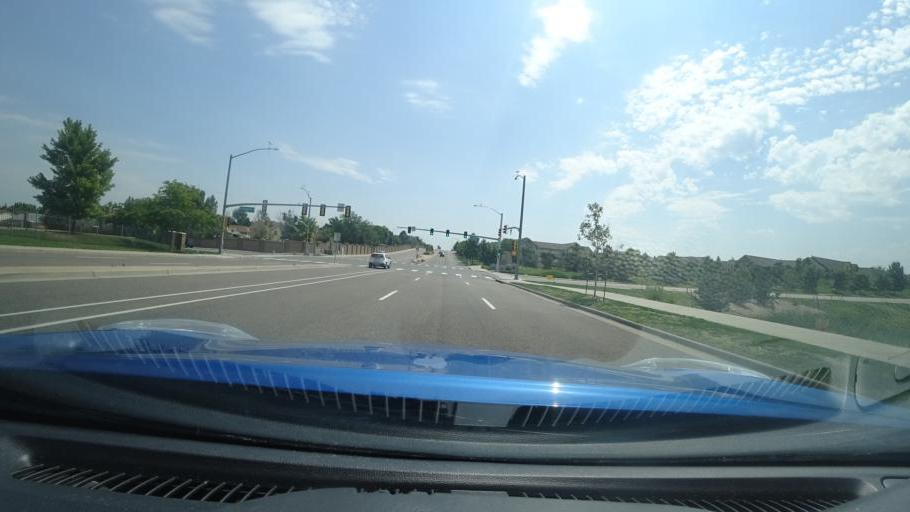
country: US
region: Colorado
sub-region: Adams County
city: Aurora
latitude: 39.6820
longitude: -104.7638
